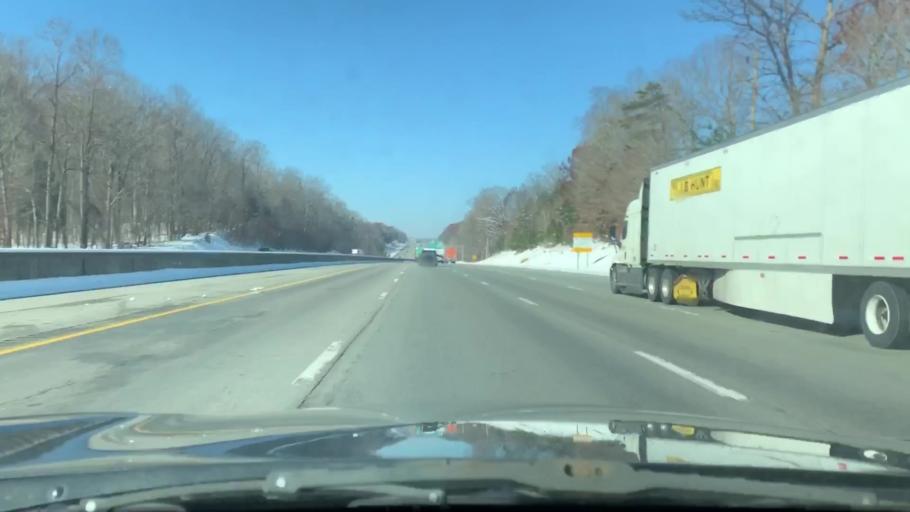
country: US
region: North Carolina
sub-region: Orange County
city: Hillsborough
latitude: 36.0631
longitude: -79.1379
